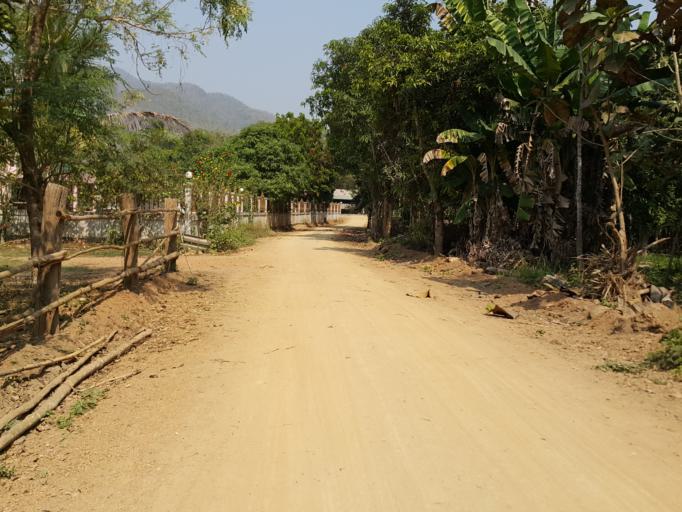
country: TH
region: Sukhothai
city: Thung Saliam
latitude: 17.3417
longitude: 99.4650
